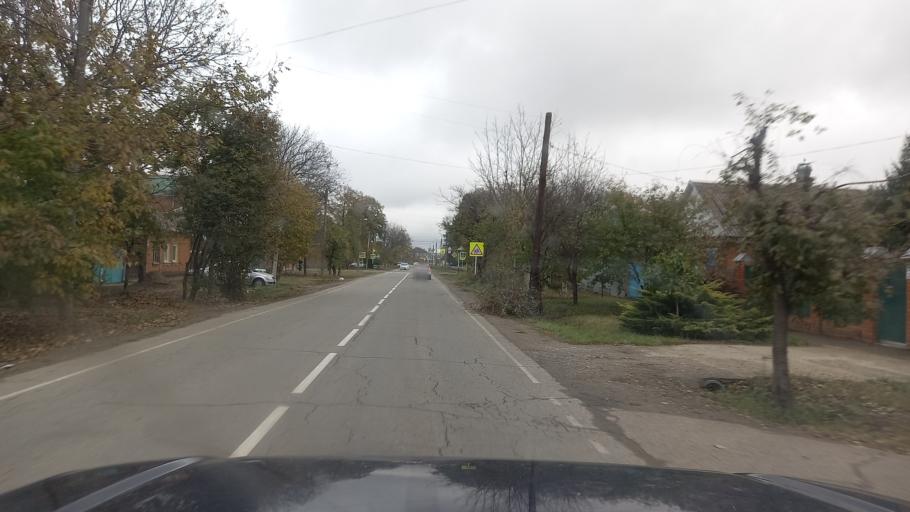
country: RU
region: Adygeya
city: Maykop
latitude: 44.6075
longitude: 40.0750
